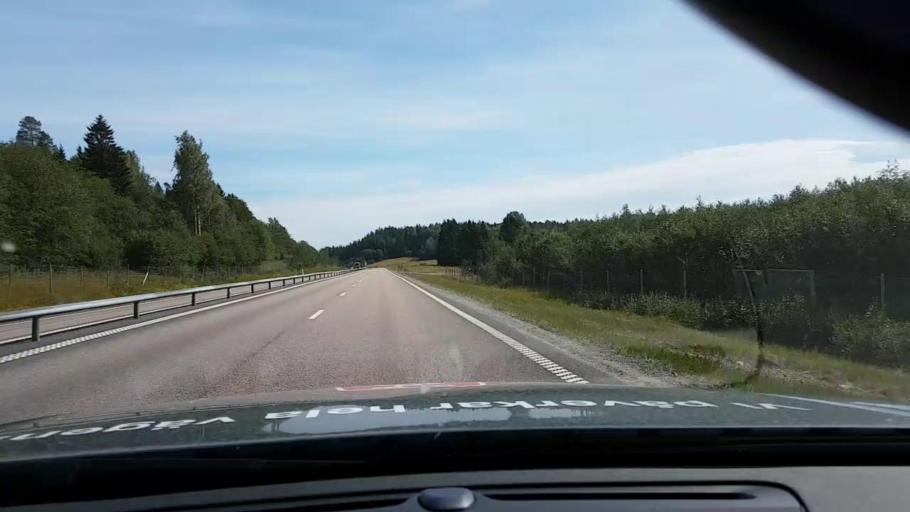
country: SE
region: Vaesternorrland
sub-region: OErnskoeldsviks Kommun
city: Ornskoldsvik
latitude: 63.3132
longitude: 18.8187
